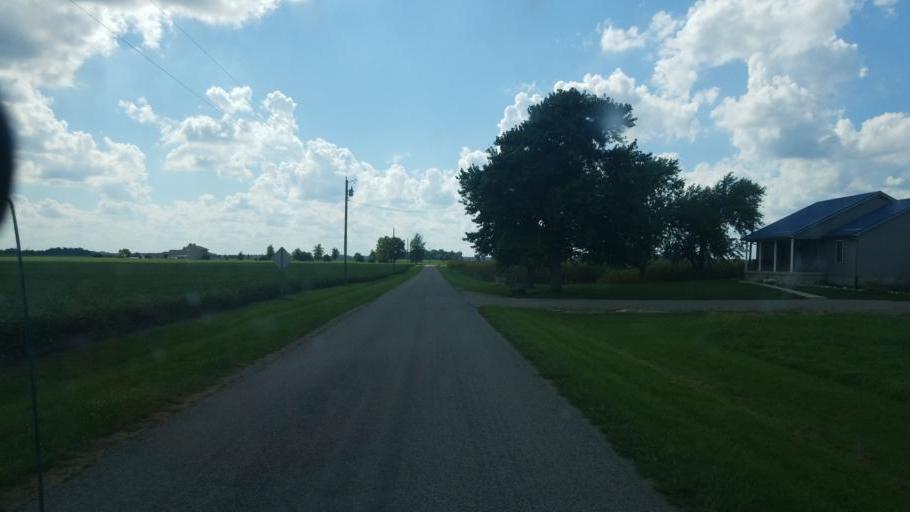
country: US
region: Ohio
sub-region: Union County
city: Richwood
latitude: 40.5009
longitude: -83.3480
